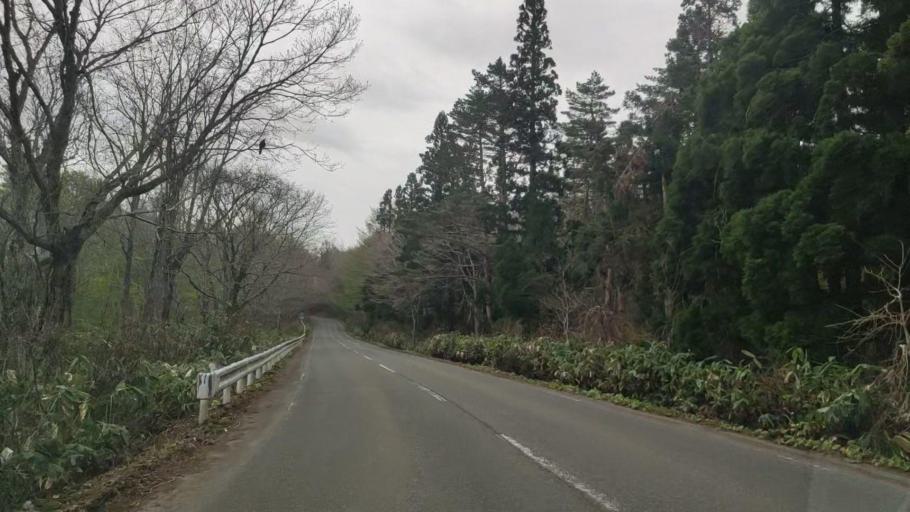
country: JP
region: Aomori
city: Aomori Shi
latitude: 40.7259
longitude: 140.8488
